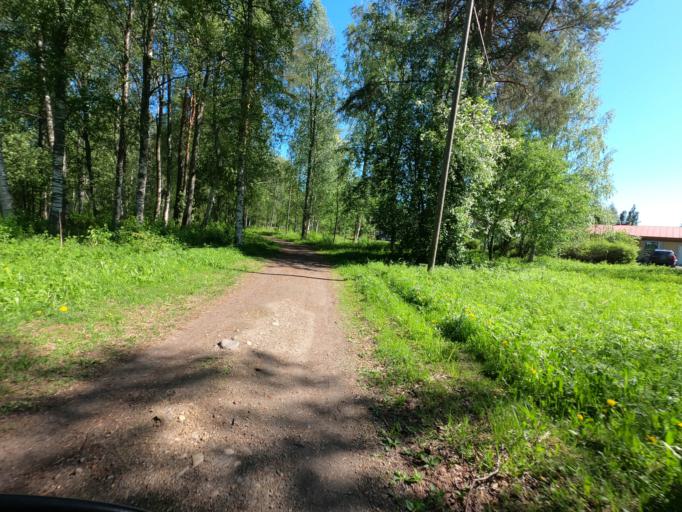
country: FI
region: North Karelia
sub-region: Joensuu
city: Joensuu
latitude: 62.6063
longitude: 29.8084
